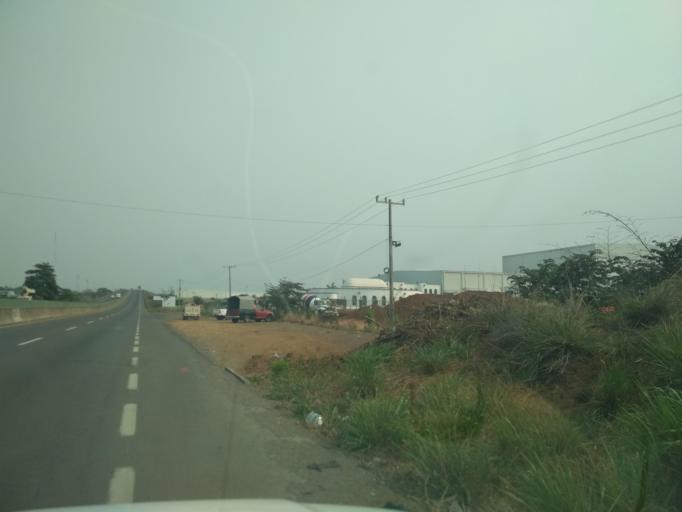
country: MX
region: Veracruz
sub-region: Veracruz
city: Delfino Victoria (Santa Fe)
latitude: 19.1709
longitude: -96.2674
